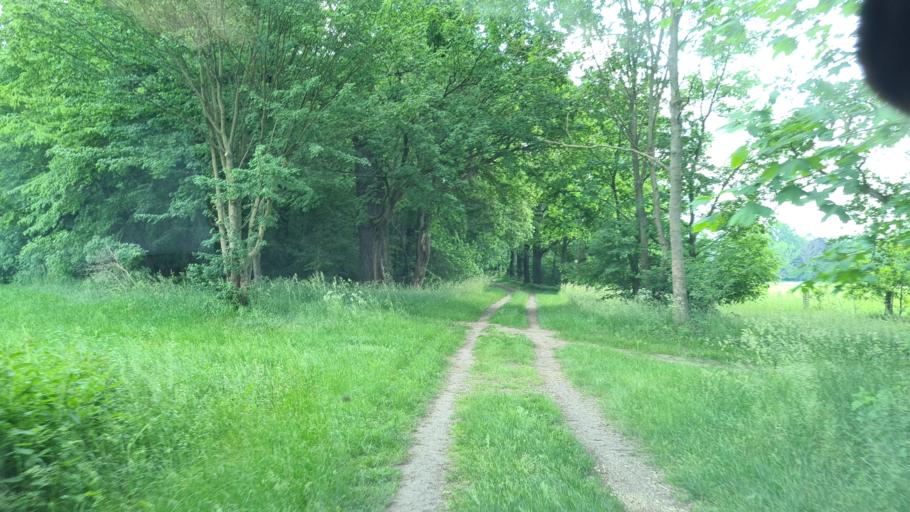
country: DE
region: Brandenburg
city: Sonnewalde
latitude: 51.7007
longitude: 13.6387
